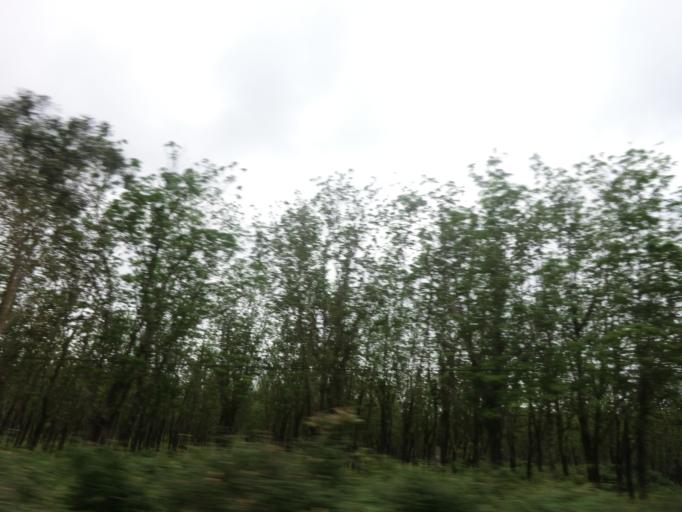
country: VN
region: Quang Tri
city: Cam Lo
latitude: 16.9014
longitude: 106.9816
